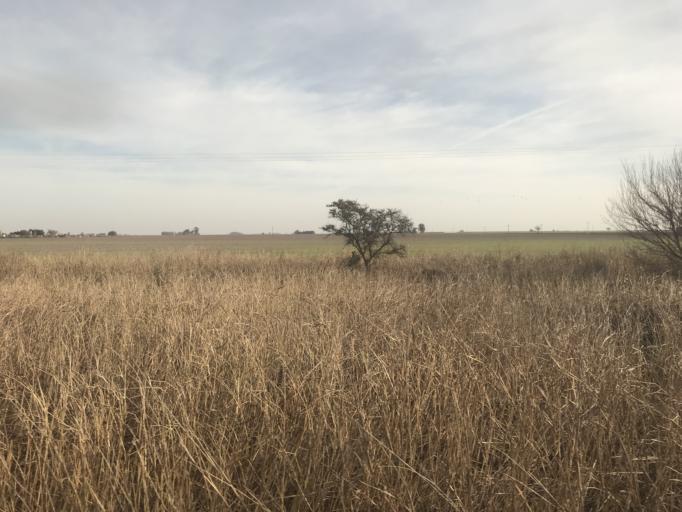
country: AR
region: Cordoba
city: Laguna Larga
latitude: -31.7531
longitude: -63.8239
